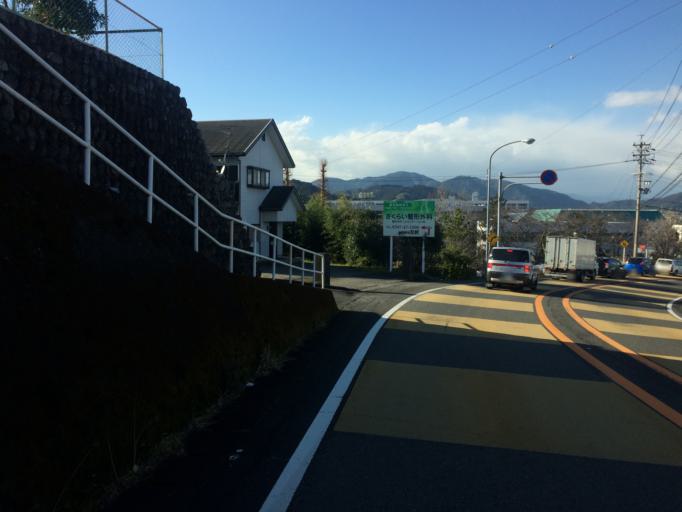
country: JP
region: Shizuoka
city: Kanaya
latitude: 34.8253
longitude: 138.1284
